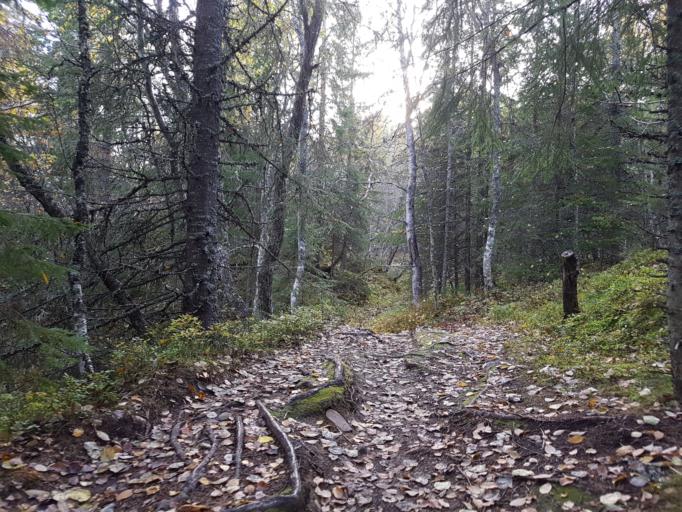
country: NO
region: Sor-Trondelag
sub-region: Trondheim
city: Trondheim
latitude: 63.4458
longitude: 10.2806
